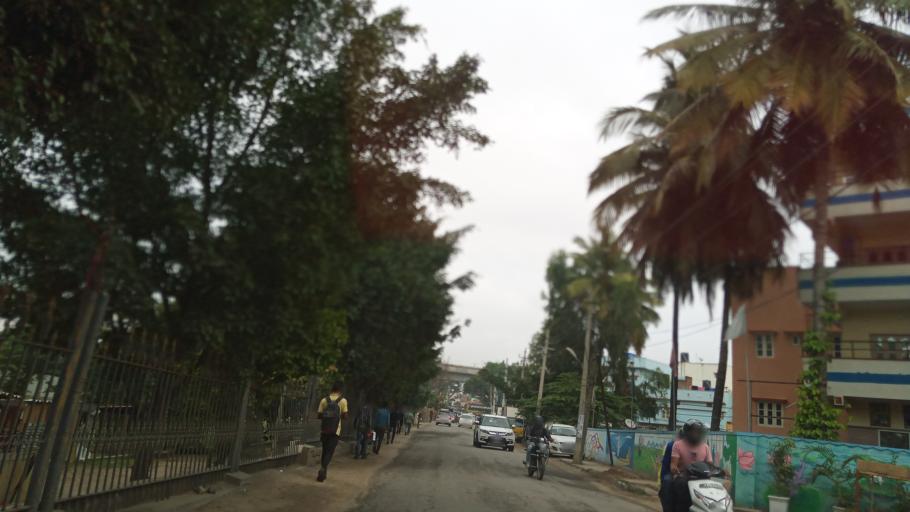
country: IN
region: Karnataka
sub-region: Bangalore Urban
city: Bangalore
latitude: 12.9113
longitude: 77.4862
